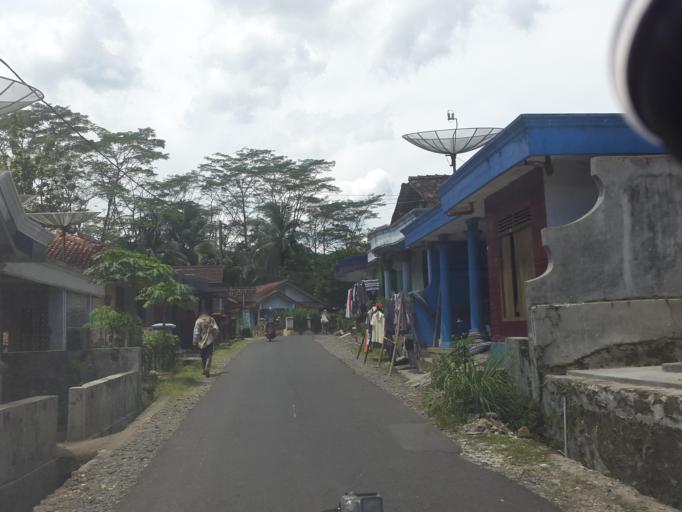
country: ID
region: Central Java
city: Sangkalputung
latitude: -7.4180
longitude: 109.0446
